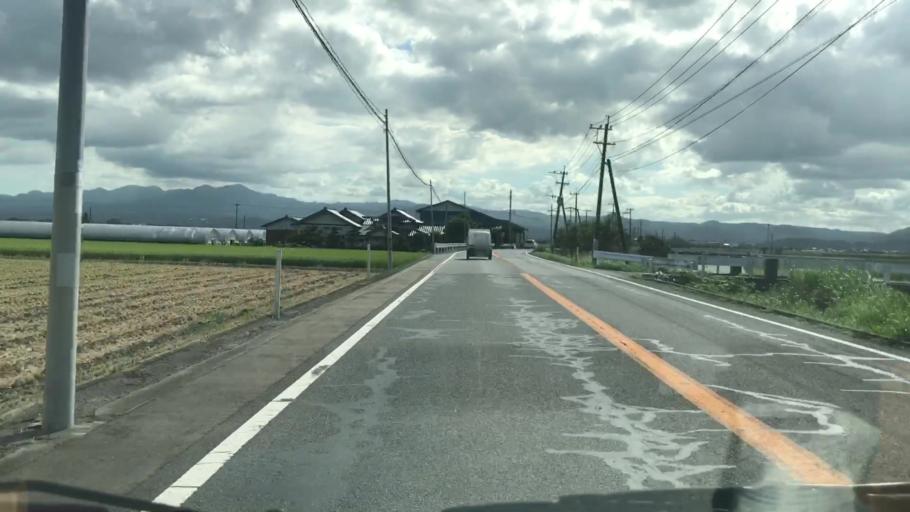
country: JP
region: Saga Prefecture
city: Kashima
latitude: 33.1588
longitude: 130.1630
